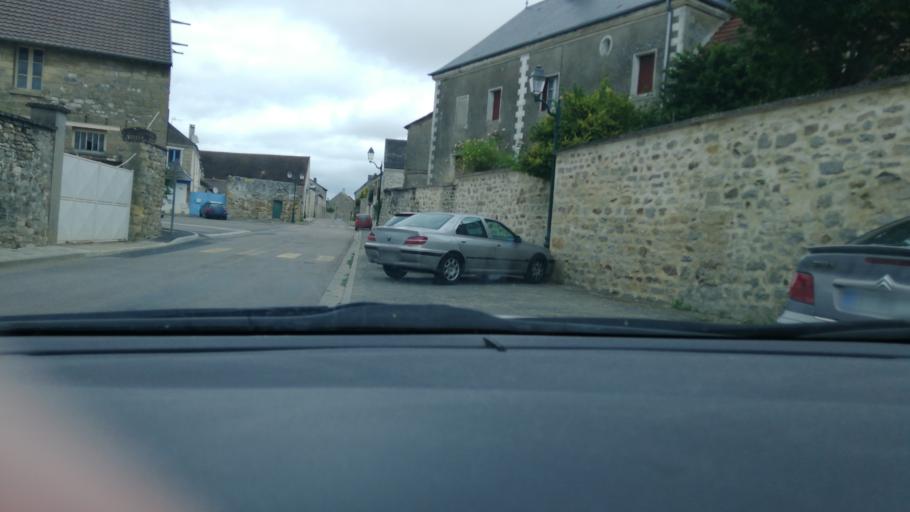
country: FR
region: Ile-de-France
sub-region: Departement du Val-d'Oise
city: Osny
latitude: 49.0887
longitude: 2.0678
